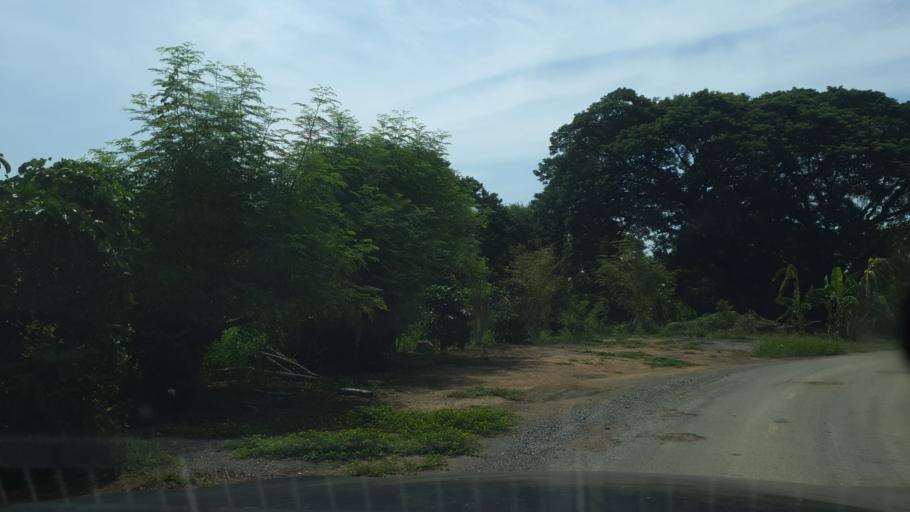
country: TH
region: Sukhothai
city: Sawankhalok
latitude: 17.2177
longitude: 99.7172
